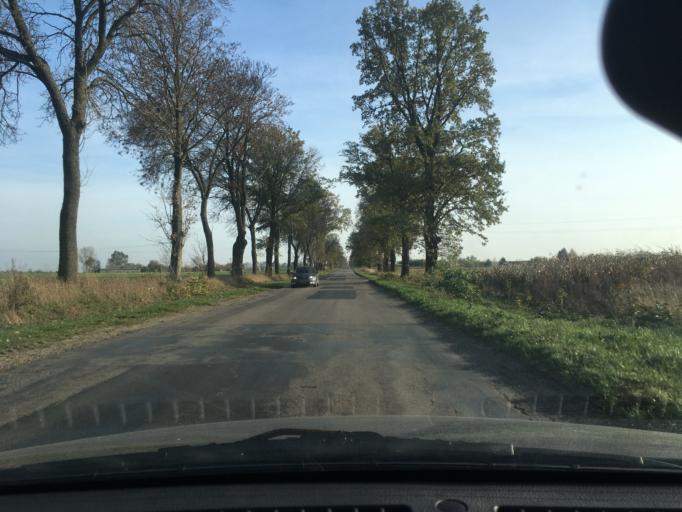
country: PL
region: Masovian Voivodeship
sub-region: Powiat plocki
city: Bodzanow
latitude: 52.4857
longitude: 20.0577
